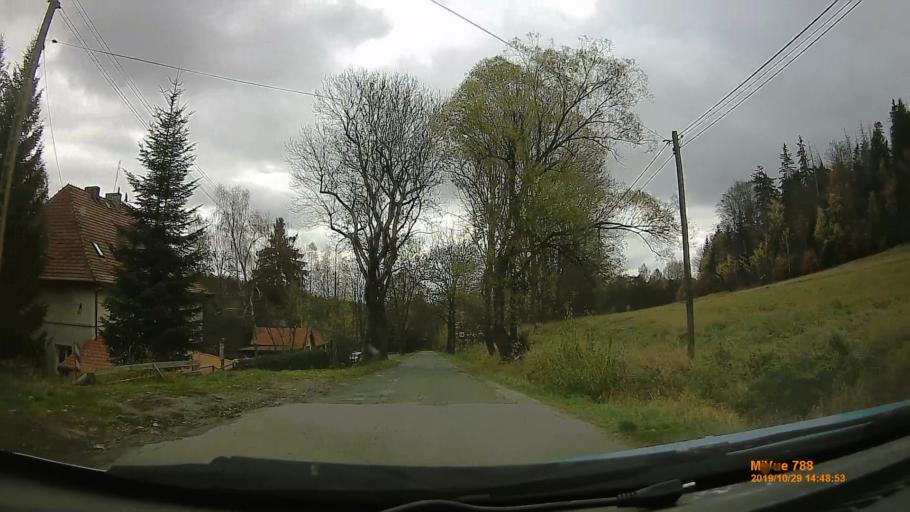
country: PL
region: Lower Silesian Voivodeship
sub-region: Powiat klodzki
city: Szczytna
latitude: 50.4349
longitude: 16.4303
